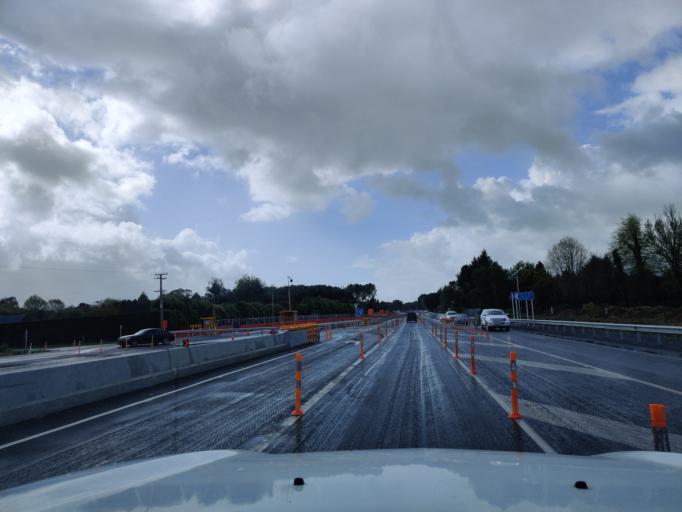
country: NZ
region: Waikato
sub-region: Hamilton City
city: Hamilton
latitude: -37.8223
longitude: 175.3496
